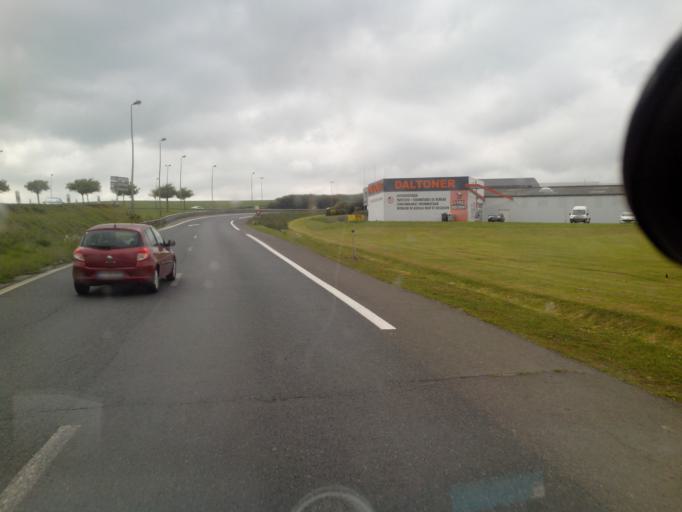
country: FR
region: Lower Normandy
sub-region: Departement du Calvados
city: Bretteville-sur-Odon
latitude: 49.1653
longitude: -0.4264
